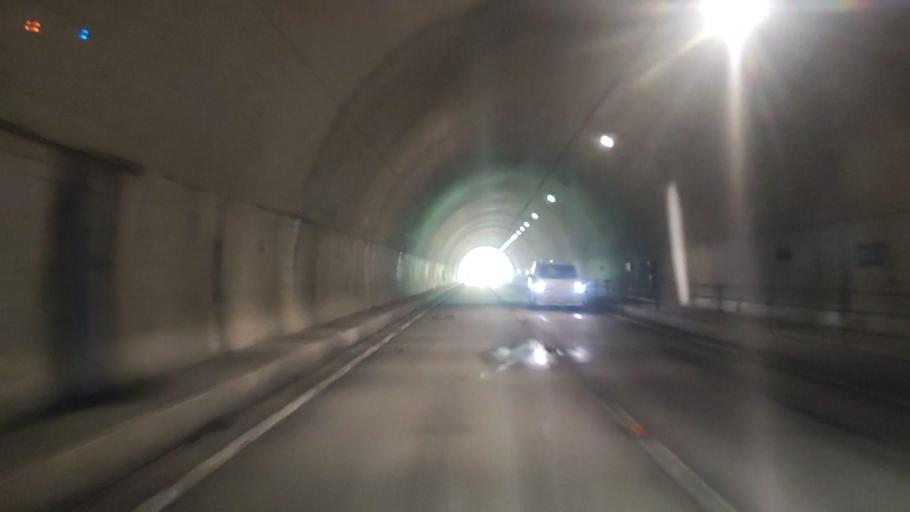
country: JP
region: Miyazaki
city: Nobeoka
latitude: 32.7384
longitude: 131.8246
